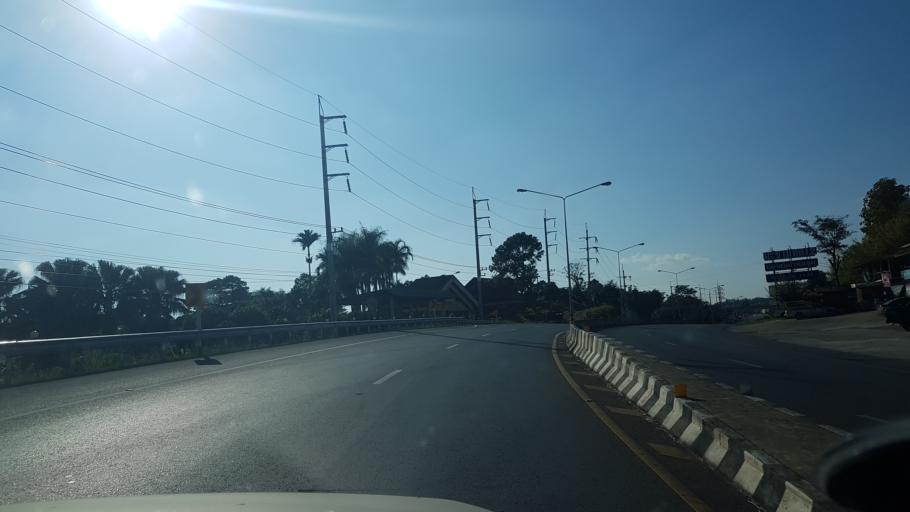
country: TH
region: Phetchabun
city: Khao Kho
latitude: 16.7688
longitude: 101.0541
